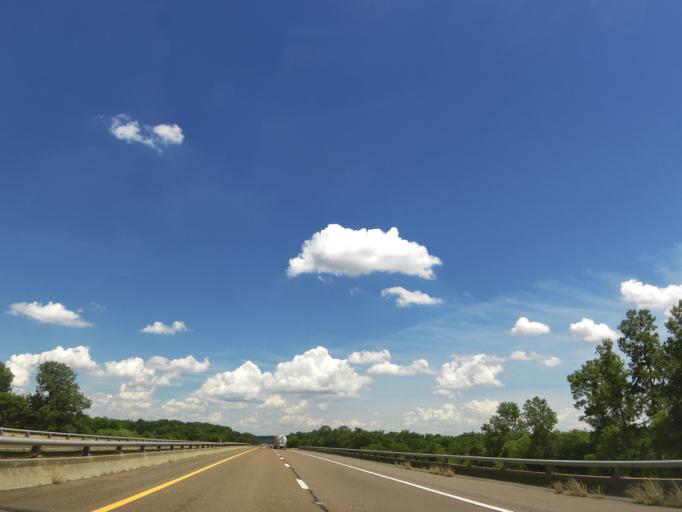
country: US
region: Missouri
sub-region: Pemiscot County
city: Caruthersville
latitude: 36.0854
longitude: -89.5510
